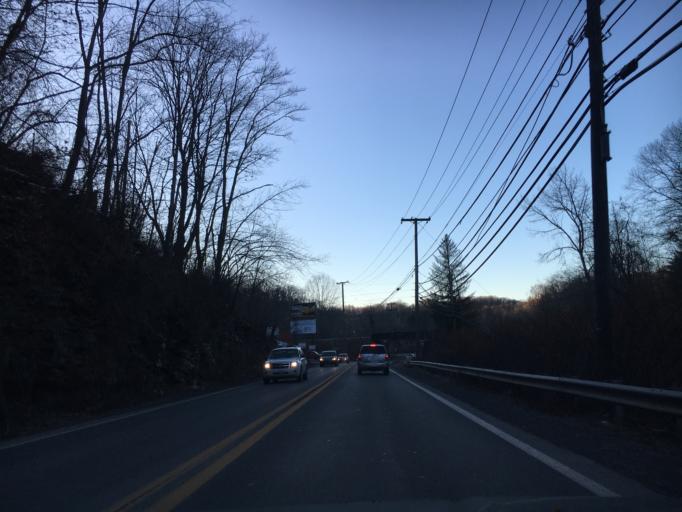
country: US
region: West Virginia
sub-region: Raleigh County
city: Beaver
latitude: 37.7561
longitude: -81.1548
